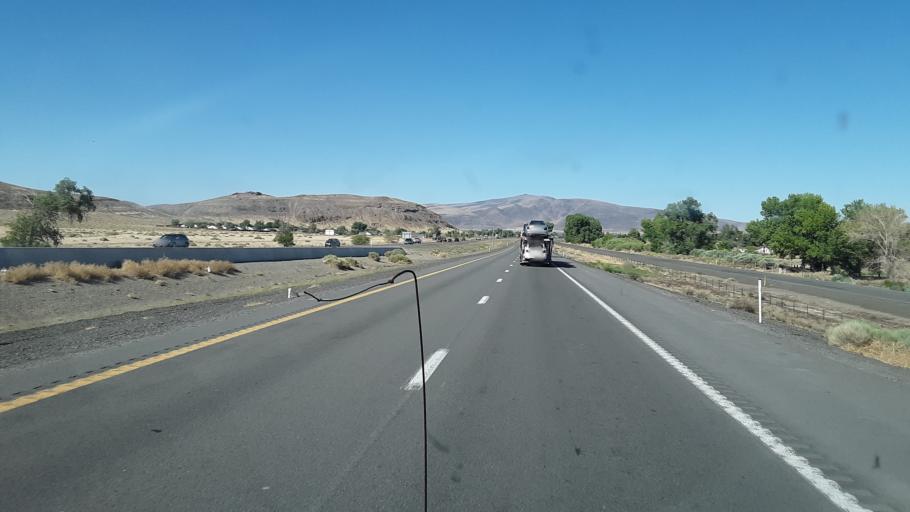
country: US
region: Nevada
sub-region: Lyon County
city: Fernley
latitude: 39.6092
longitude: -119.3197
